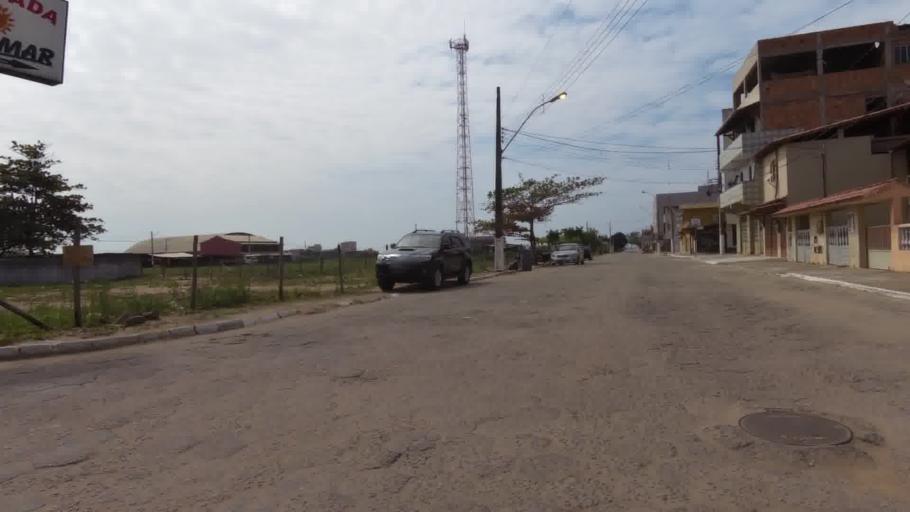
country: BR
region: Espirito Santo
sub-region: Marataizes
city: Marataizes
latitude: -21.0248
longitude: -40.8164
